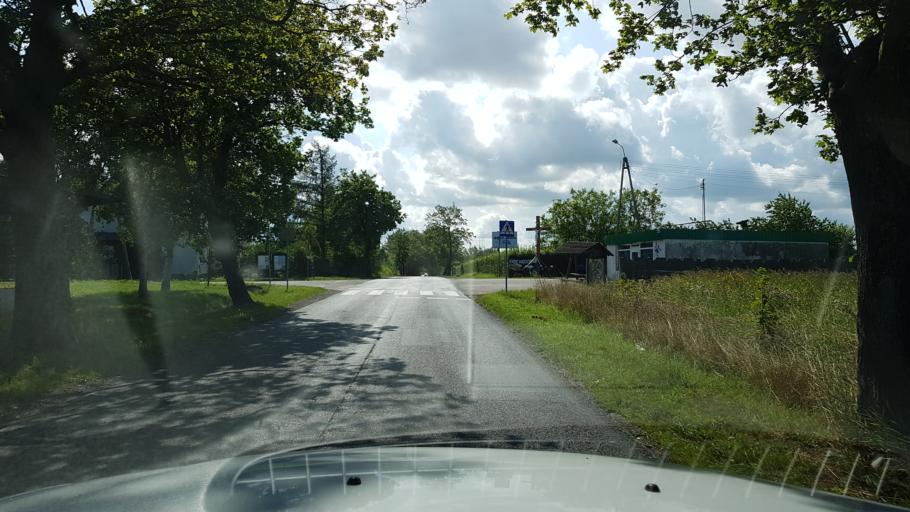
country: PL
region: West Pomeranian Voivodeship
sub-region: Powiat kolobrzeski
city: Ustronie Morskie
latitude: 54.1828
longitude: 15.7439
